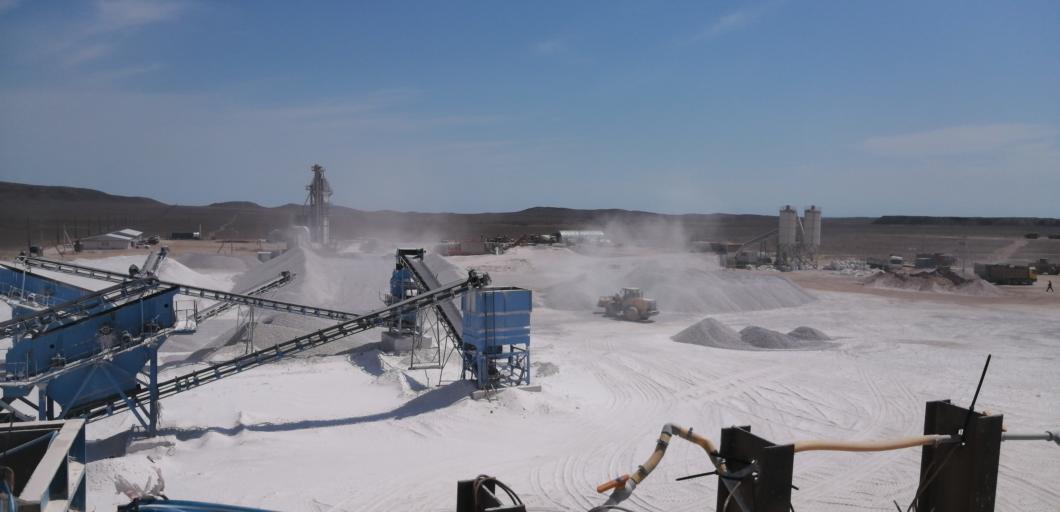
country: KZ
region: Qaraghandy
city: Balqash
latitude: 46.6291
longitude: 74.3753
